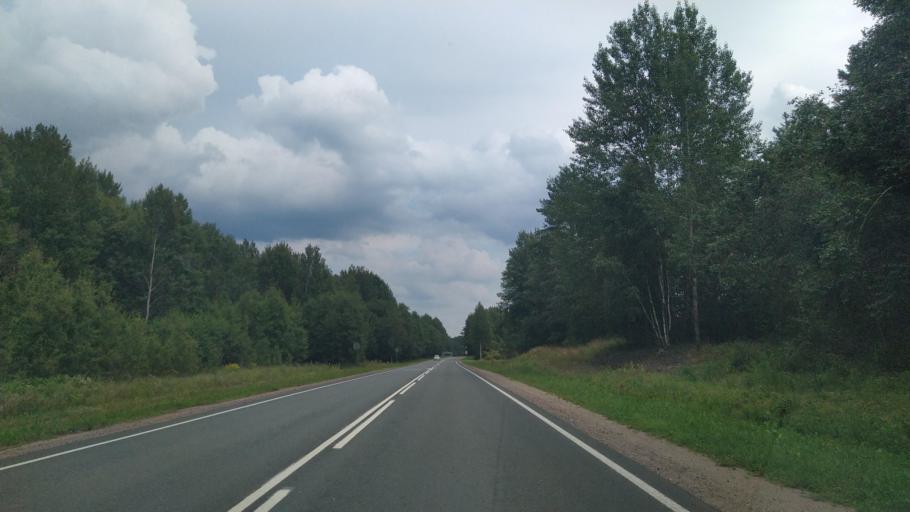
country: RU
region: Pskov
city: Pskov
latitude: 57.8333
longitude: 28.5219
